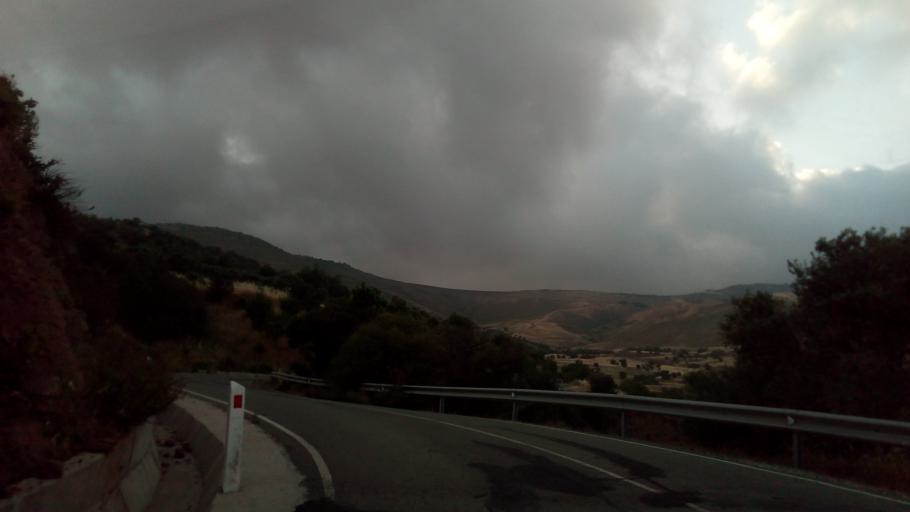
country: CY
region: Limassol
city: Pachna
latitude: 34.8658
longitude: 32.6408
